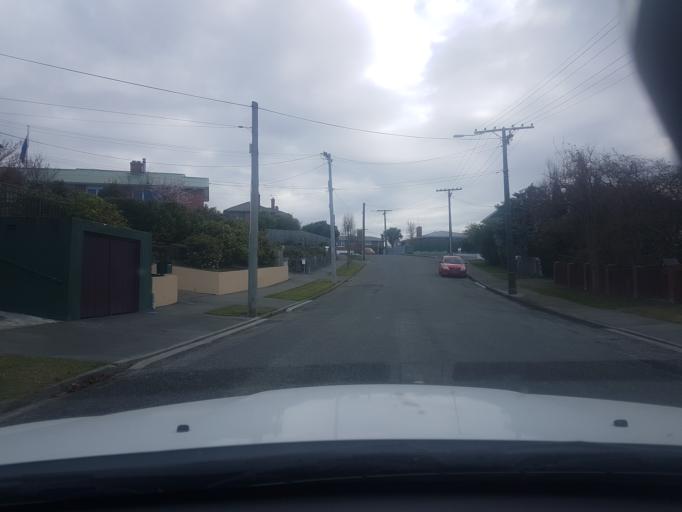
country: NZ
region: Canterbury
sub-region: Timaru District
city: Timaru
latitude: -44.3920
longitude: 171.2169
